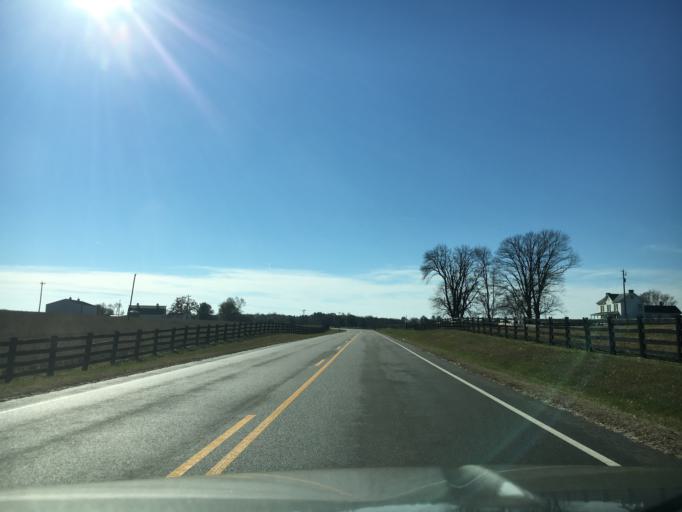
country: US
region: Virginia
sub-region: Cumberland County
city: Cumberland
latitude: 37.5766
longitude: -78.1758
